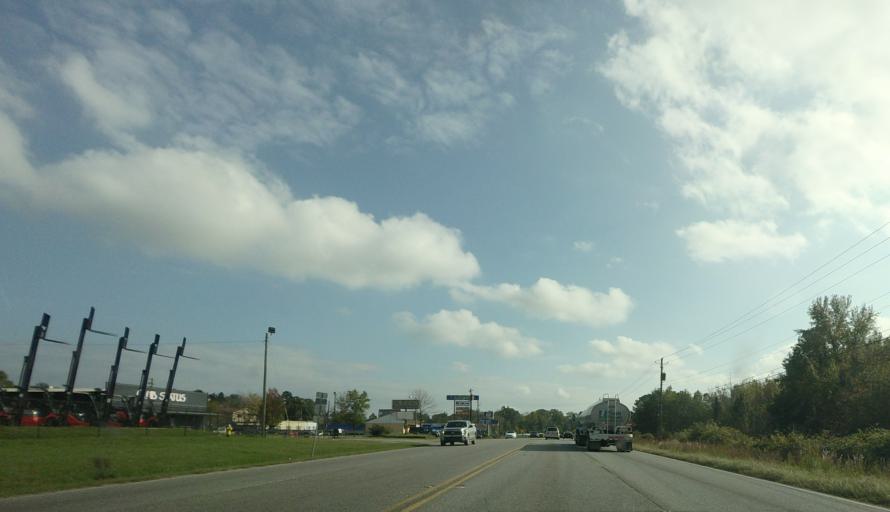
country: US
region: Georgia
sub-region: Bibb County
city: Macon
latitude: 32.7747
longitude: -83.6606
